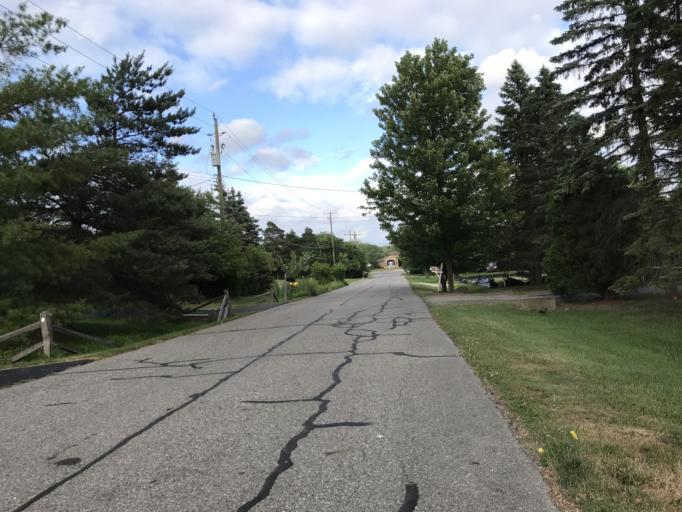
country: US
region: Michigan
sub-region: Oakland County
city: Farmington Hills
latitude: 42.4772
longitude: -83.3398
